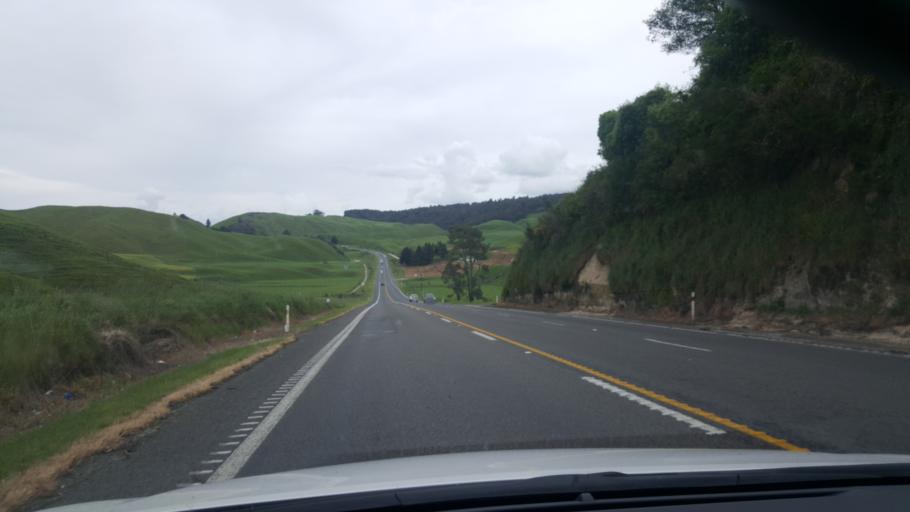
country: NZ
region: Bay of Plenty
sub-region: Rotorua District
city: Rotorua
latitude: -38.2520
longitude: 176.3183
